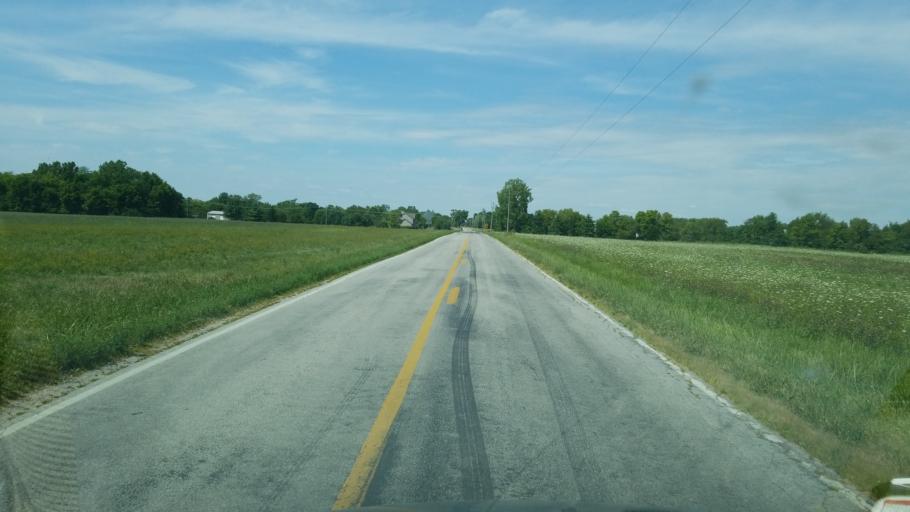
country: US
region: Ohio
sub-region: Marion County
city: Prospect
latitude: 40.3469
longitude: -83.1769
